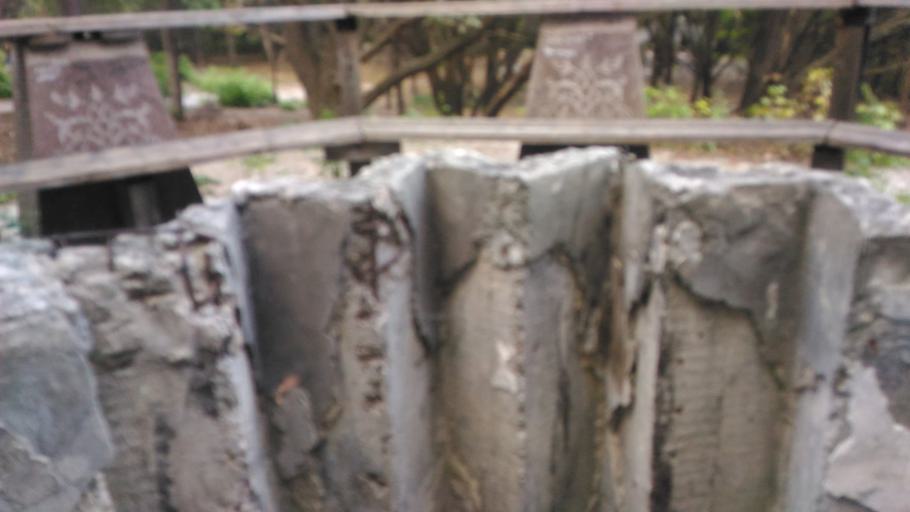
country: RU
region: Ulyanovsk
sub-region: Ulyanovskiy Rayon
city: Ulyanovsk
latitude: 54.3160
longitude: 48.4151
